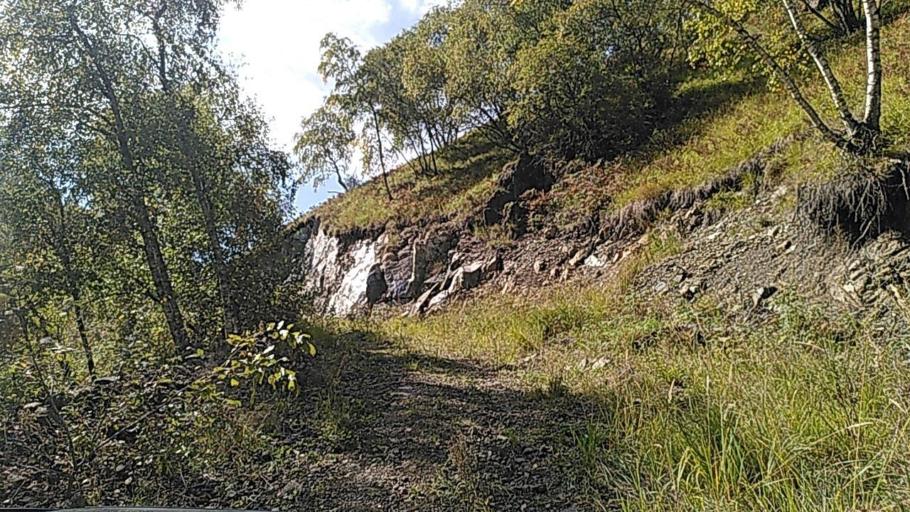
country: RU
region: Kabardino-Balkariya
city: Kamennomostskoye
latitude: 43.6886
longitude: 42.8283
